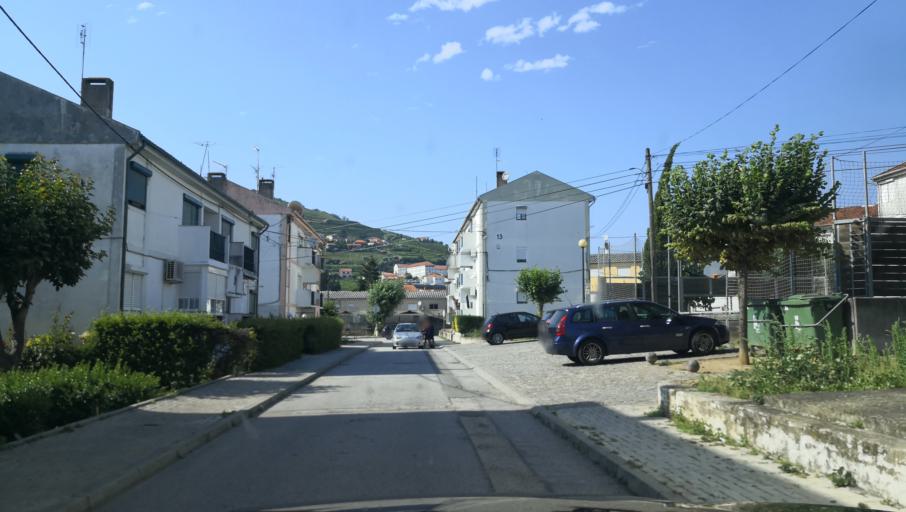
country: PT
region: Vila Real
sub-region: Peso da Regua
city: Godim
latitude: 41.1659
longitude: -7.8037
